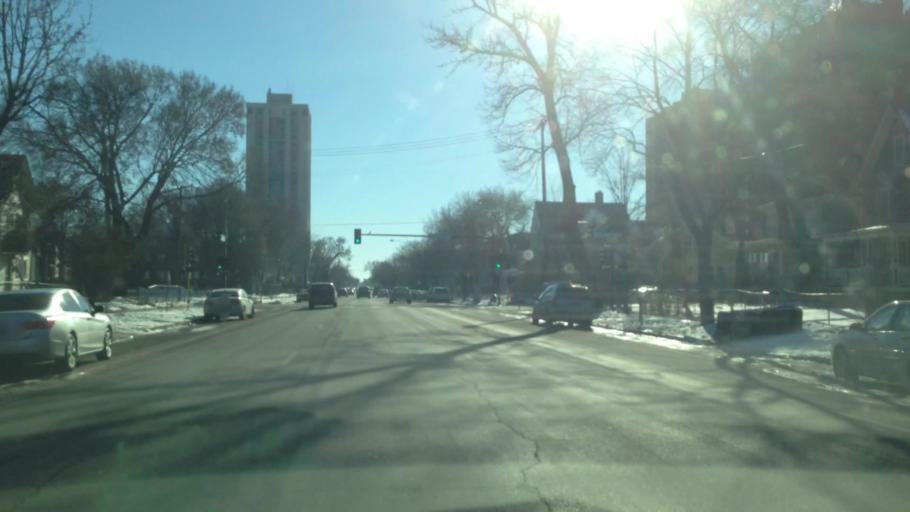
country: US
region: Minnesota
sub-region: Hennepin County
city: Minneapolis
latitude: 44.9599
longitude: -93.2677
